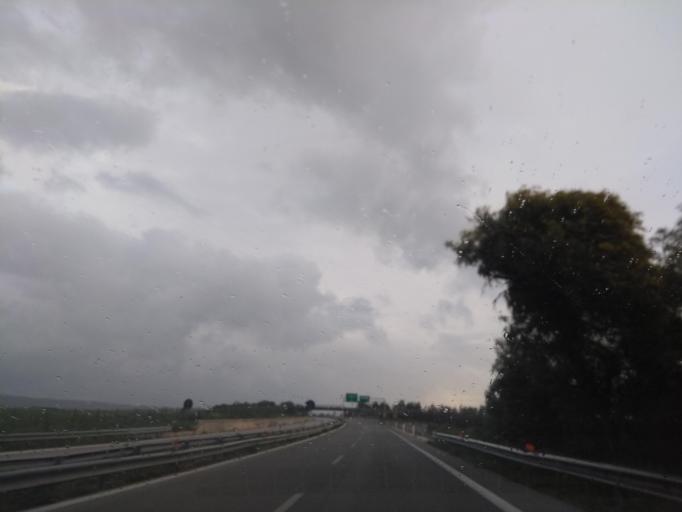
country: IT
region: Sicily
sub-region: Trapani
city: Paceco
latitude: 37.9664
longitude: 12.6191
